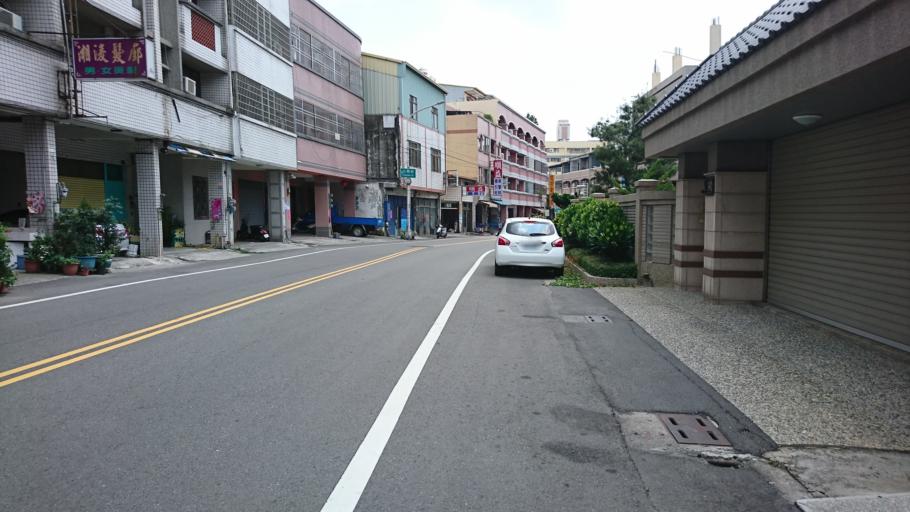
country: TW
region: Taiwan
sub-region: Taichung City
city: Taichung
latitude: 24.0798
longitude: 120.6961
